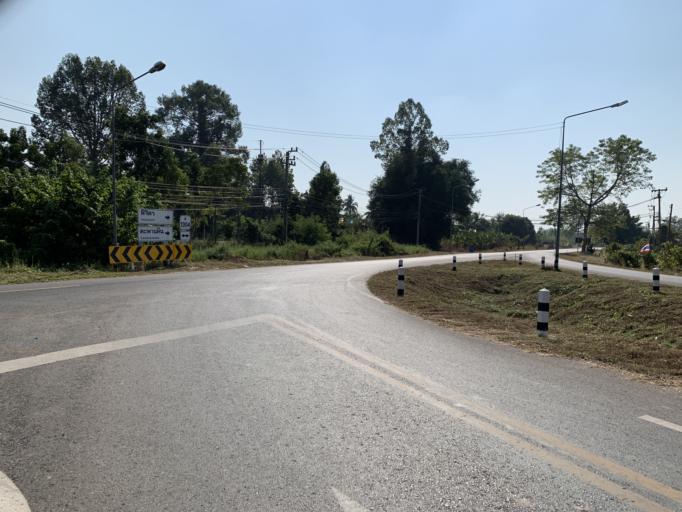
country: TH
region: Phichit
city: Phichit
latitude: 16.3440
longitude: 100.3926
